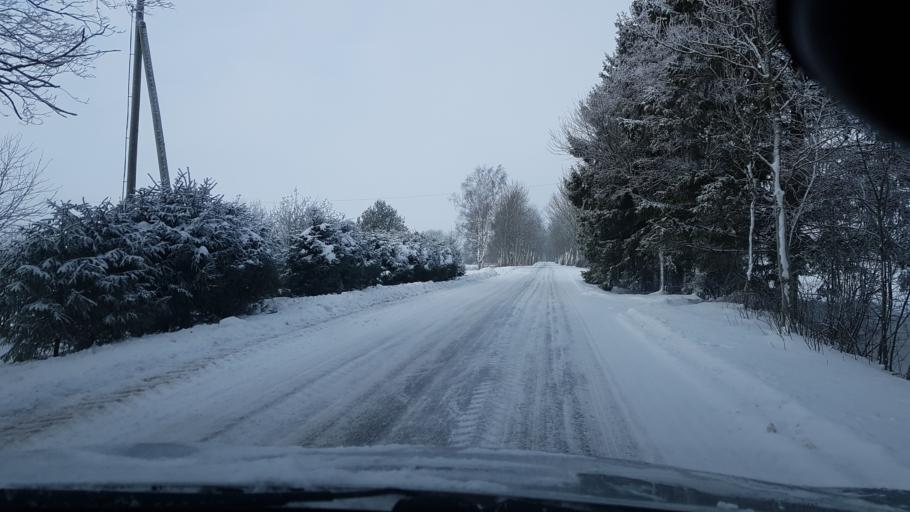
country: EE
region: Harju
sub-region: Keila linn
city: Keila
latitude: 59.3277
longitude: 24.4479
